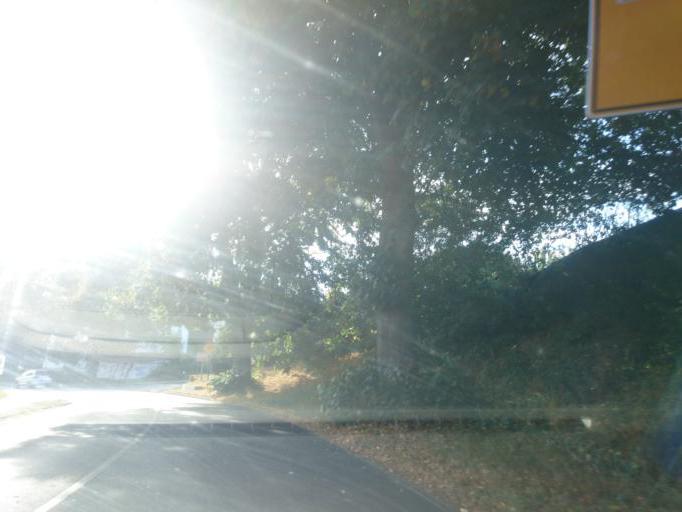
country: DE
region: Mecklenburg-Vorpommern
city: Bad Doberan
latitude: 54.1108
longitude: 11.9070
